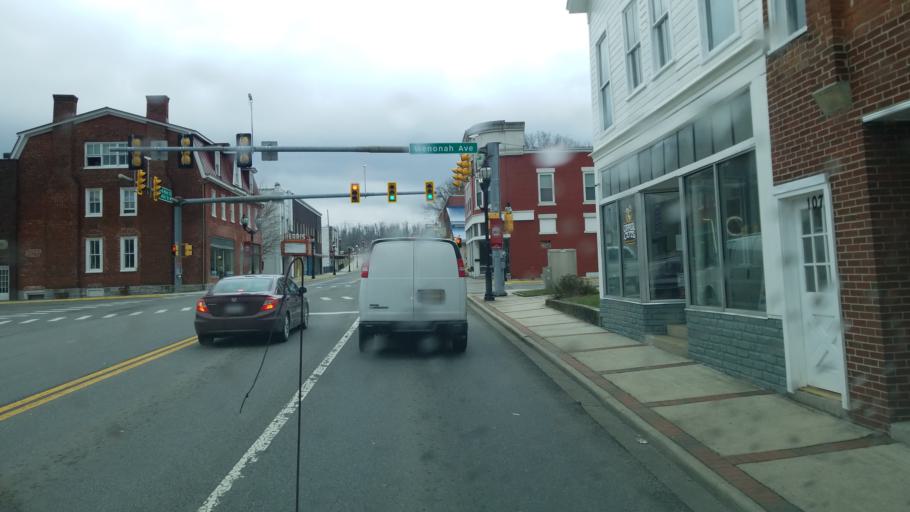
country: US
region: Virginia
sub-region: Giles County
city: Pearisburg
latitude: 37.3267
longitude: -80.7353
